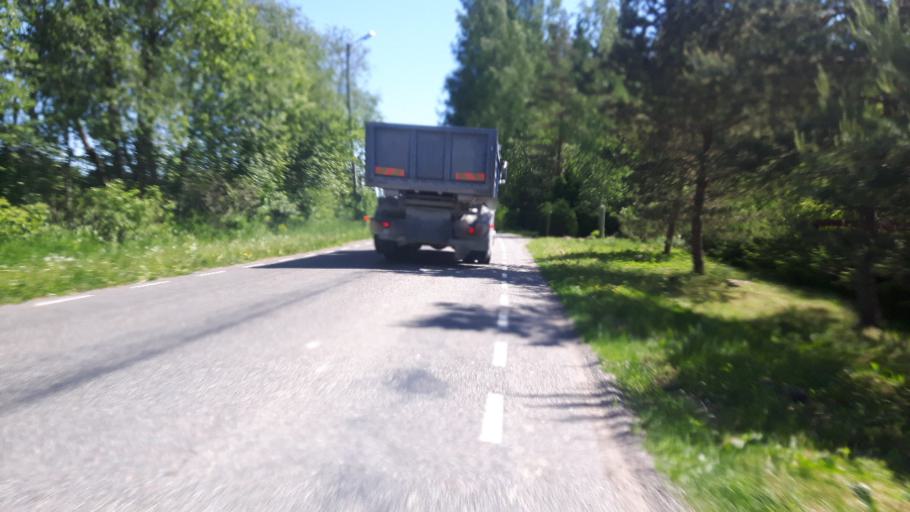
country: EE
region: Raplamaa
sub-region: Kohila vald
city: Kohila
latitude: 59.1765
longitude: 24.7292
